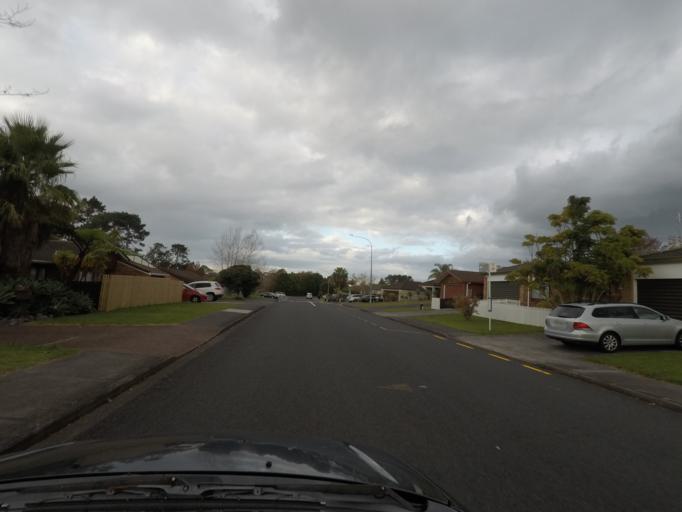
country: NZ
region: Auckland
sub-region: Auckland
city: Rosebank
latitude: -36.8289
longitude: 174.6271
